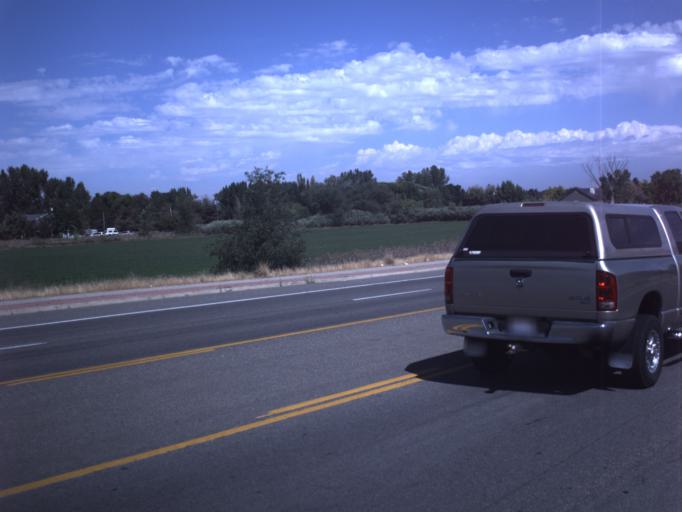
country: US
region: Utah
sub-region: Weber County
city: Marriott-Slaterville
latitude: 41.2472
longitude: -112.0252
